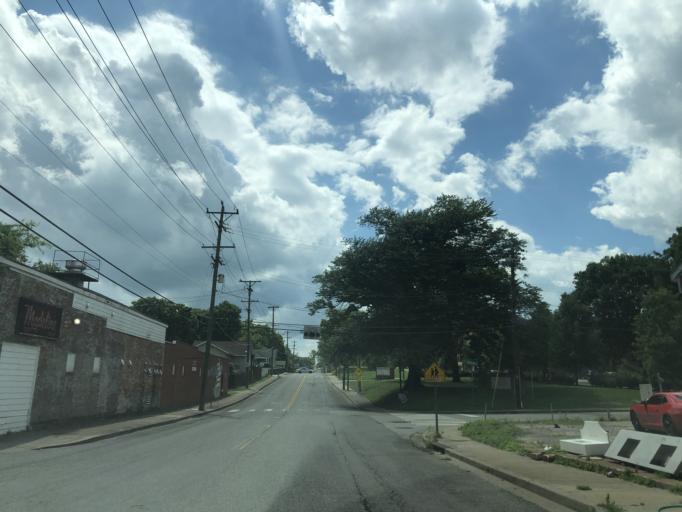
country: US
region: Tennessee
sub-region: Davidson County
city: Nashville
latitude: 36.1940
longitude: -86.7670
